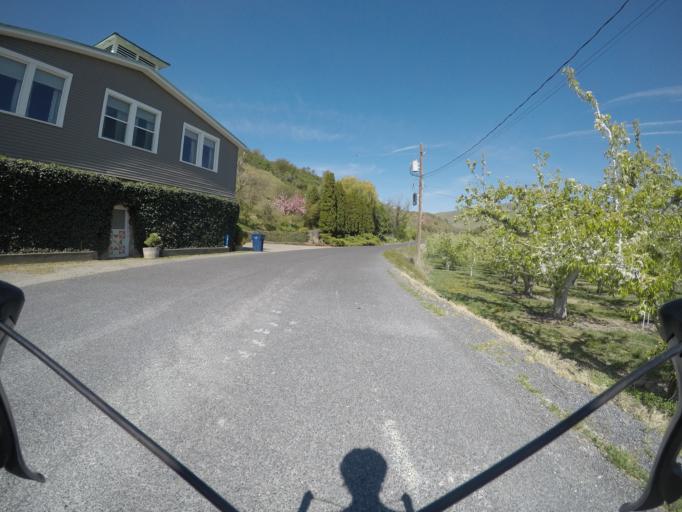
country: US
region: Washington
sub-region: Chelan County
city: West Wenatchee
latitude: 47.4717
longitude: -120.3804
